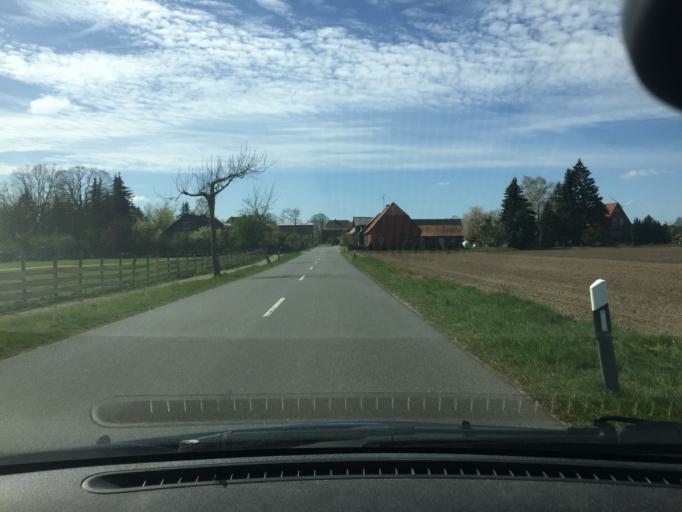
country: DE
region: Lower Saxony
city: Ratzlingen
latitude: 52.9601
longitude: 10.6690
